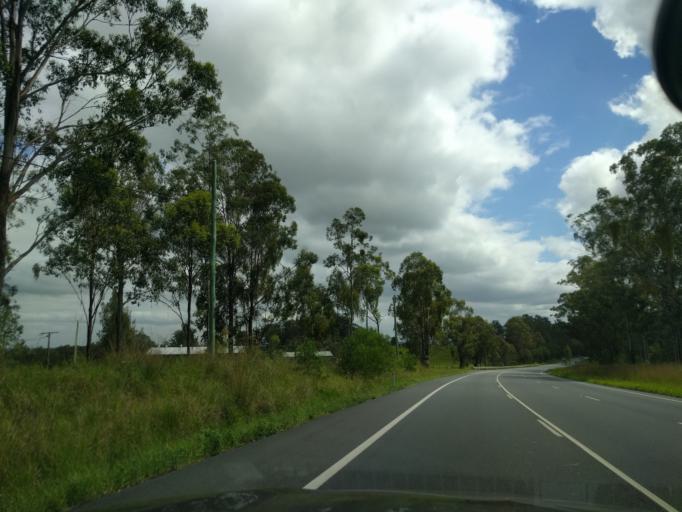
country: AU
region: Queensland
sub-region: Logan
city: Cedar Vale
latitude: -27.8764
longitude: 152.9914
